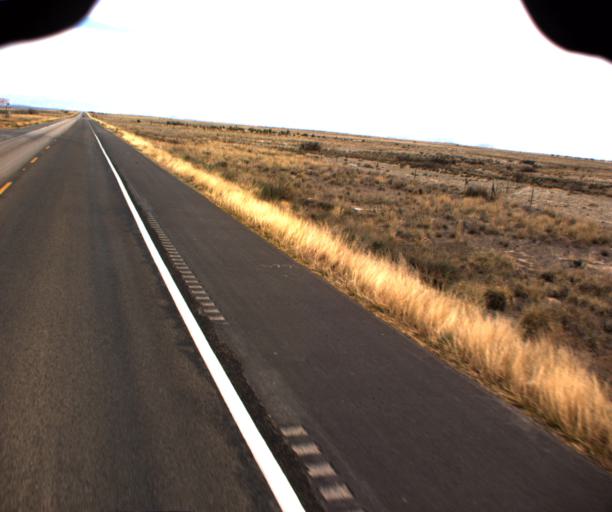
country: US
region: Arizona
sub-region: Cochise County
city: Willcox
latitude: 32.2413
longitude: -109.8141
